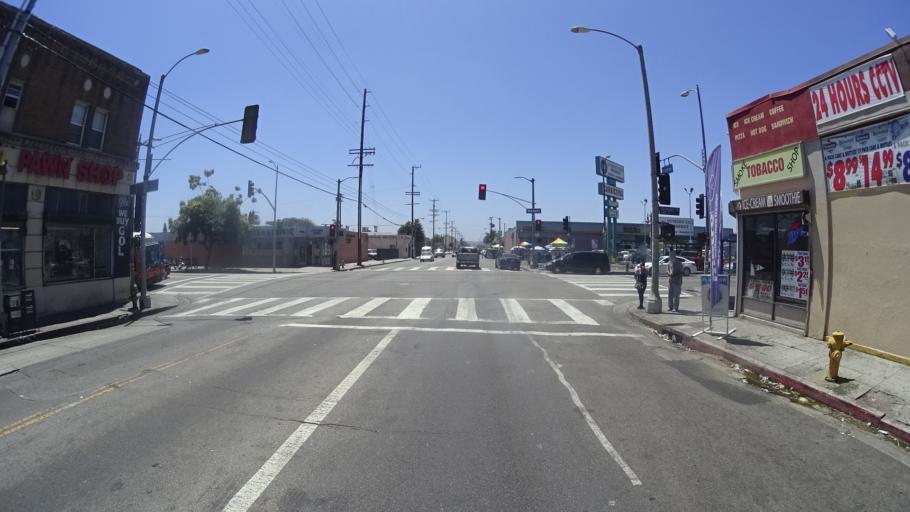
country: US
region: California
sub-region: Los Angeles County
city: View Park-Windsor Hills
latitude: 34.0037
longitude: -118.2912
